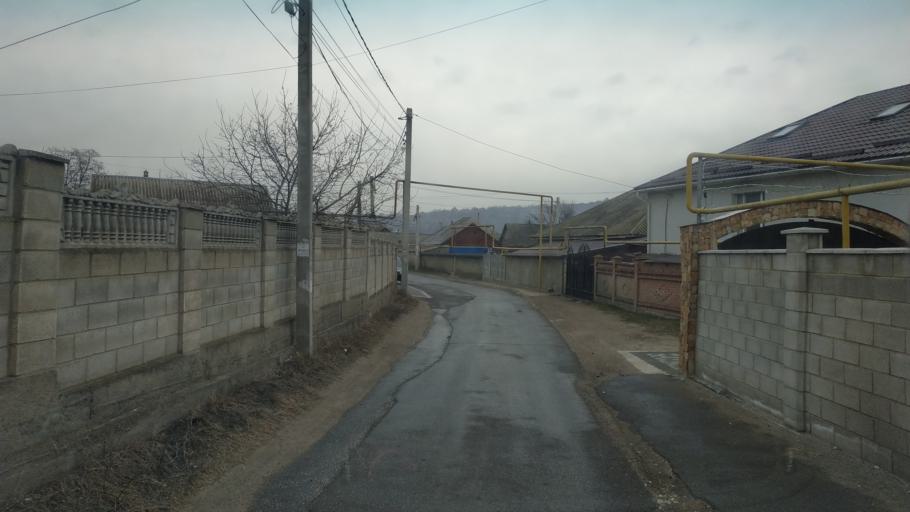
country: MD
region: Chisinau
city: Singera
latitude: 46.9141
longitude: 28.9692
